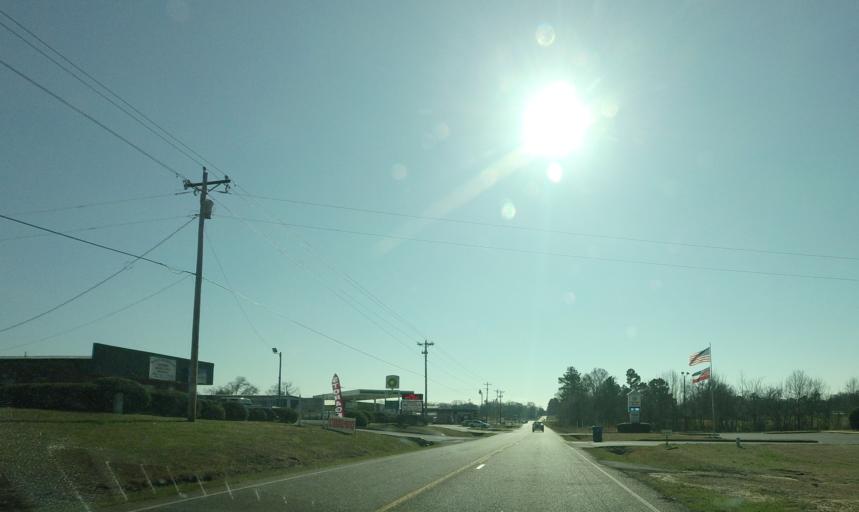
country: US
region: Tennessee
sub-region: Shelby County
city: Collierville
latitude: 34.9671
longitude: -89.6889
